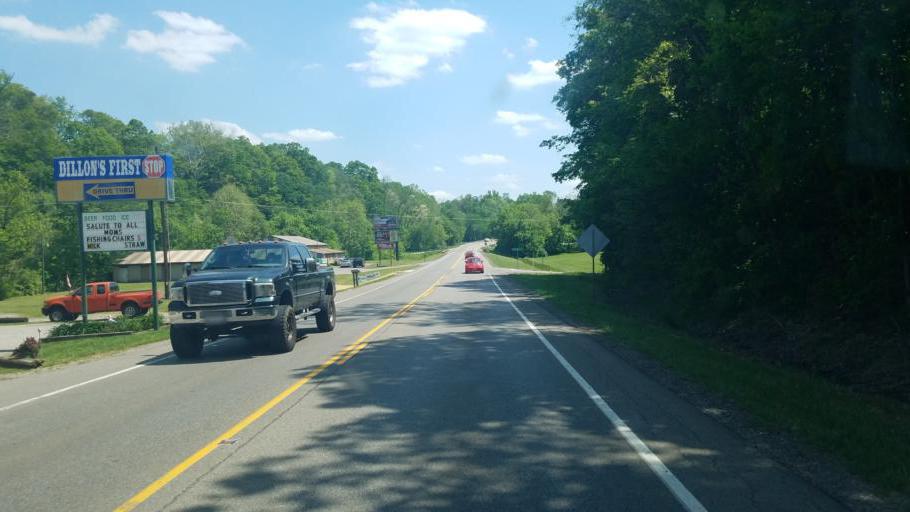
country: US
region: Ohio
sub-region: Muskingum County
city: North Zanesville
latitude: 39.9863
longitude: -82.0545
